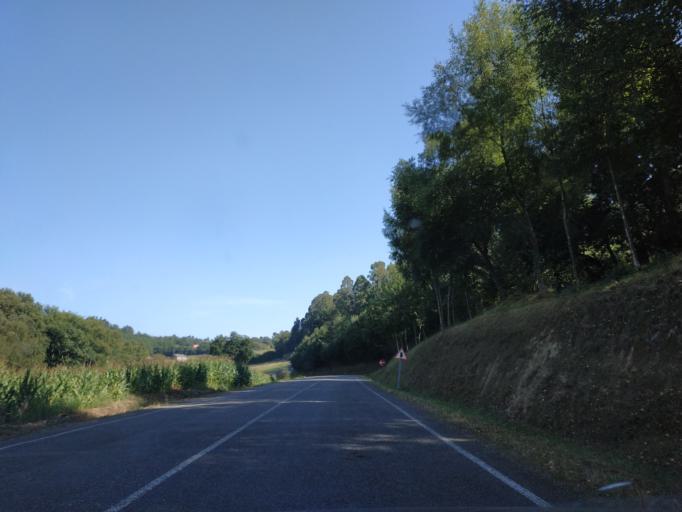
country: ES
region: Galicia
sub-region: Provincia da Coruna
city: Laracha
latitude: 43.2278
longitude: -8.5509
